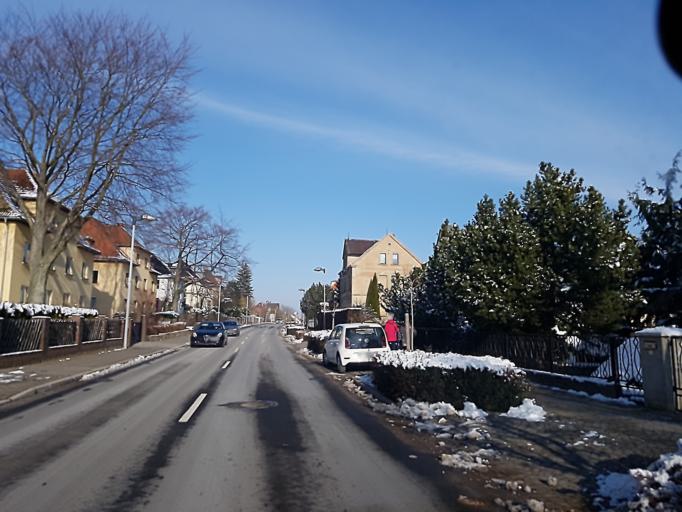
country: DE
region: Saxony
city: Leisnig
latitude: 51.1508
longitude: 12.9276
